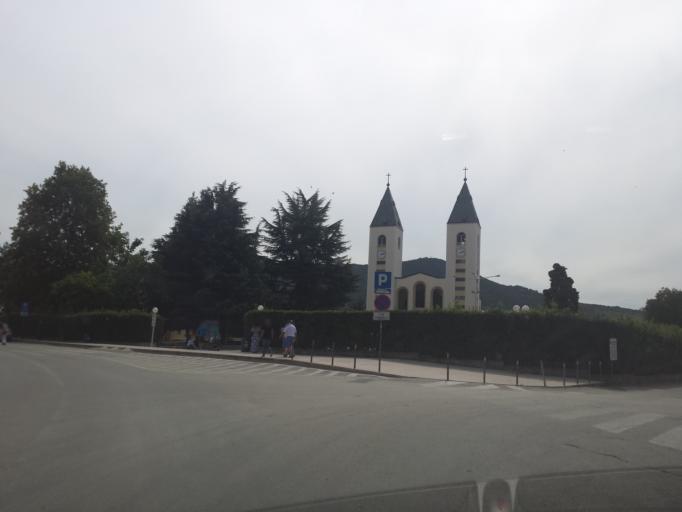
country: BA
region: Federation of Bosnia and Herzegovina
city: Citluk
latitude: 43.1916
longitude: 17.6783
